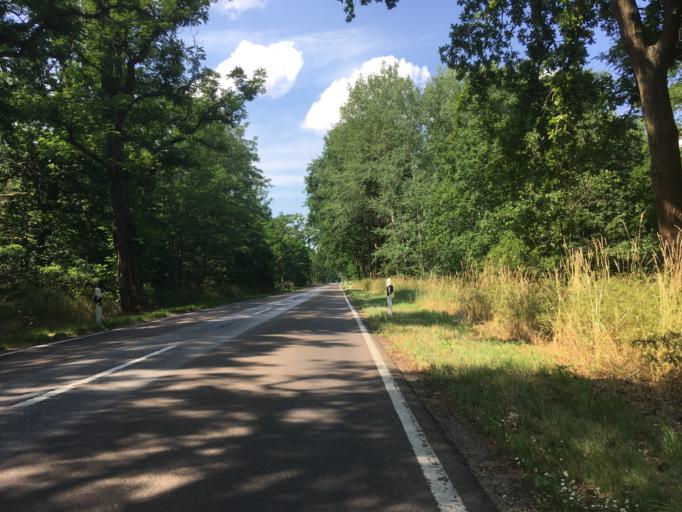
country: DE
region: Saxony-Anhalt
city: Quellendorf
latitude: 51.7882
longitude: 12.1578
